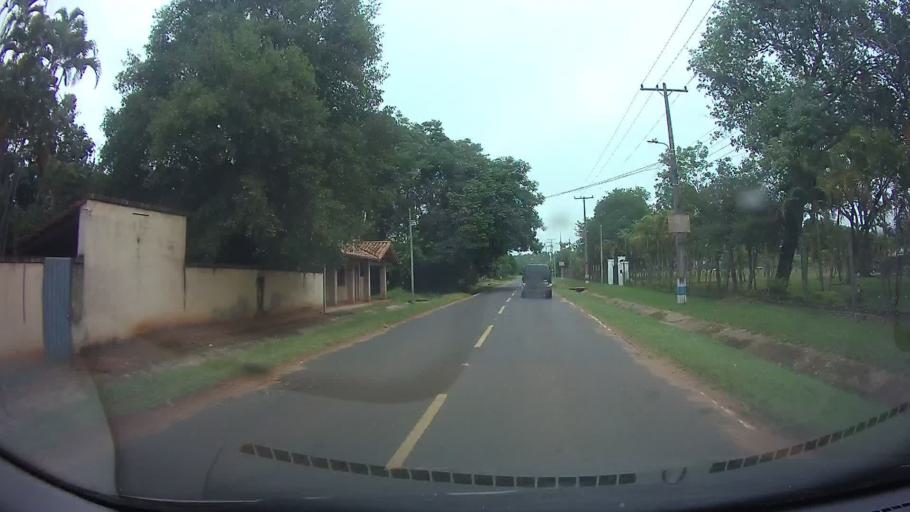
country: PY
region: Central
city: Itaugua
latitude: -25.3527
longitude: -57.3399
